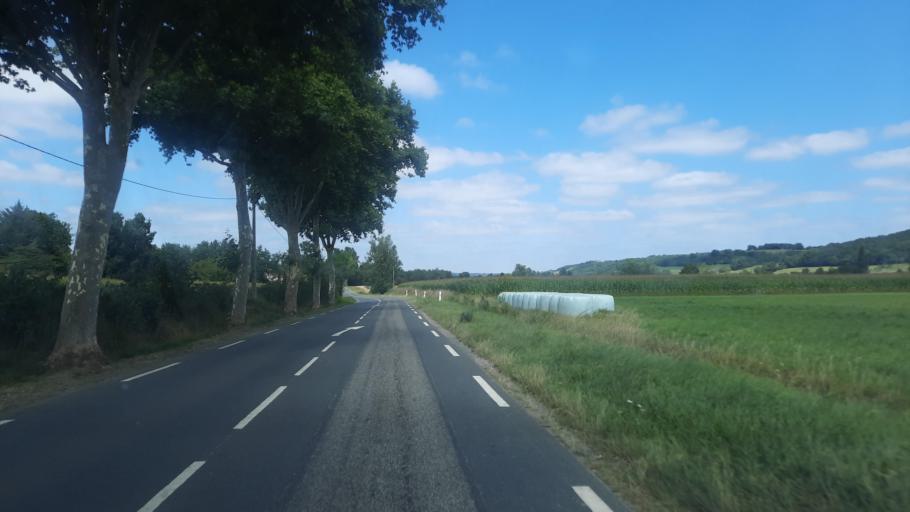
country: FR
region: Midi-Pyrenees
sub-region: Departement de la Haute-Garonne
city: Boulogne-sur-Gesse
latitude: 43.3096
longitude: 0.6789
